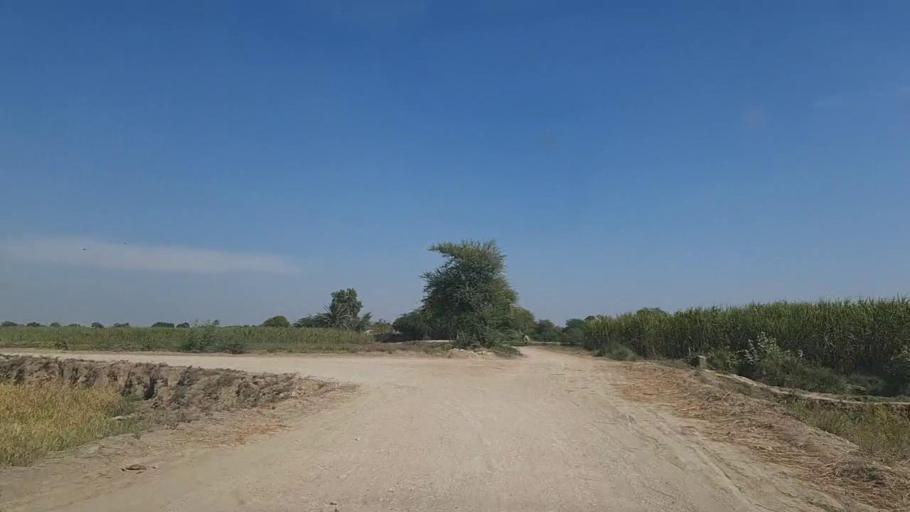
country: PK
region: Sindh
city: Mirpur Batoro
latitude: 24.7480
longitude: 68.2816
